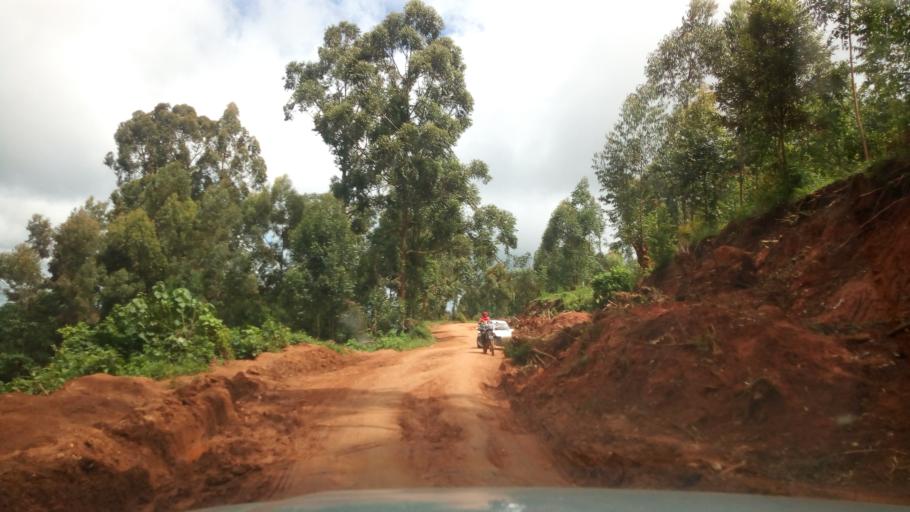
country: KE
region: Makueni
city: Wote
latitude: -1.6699
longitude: 37.4507
